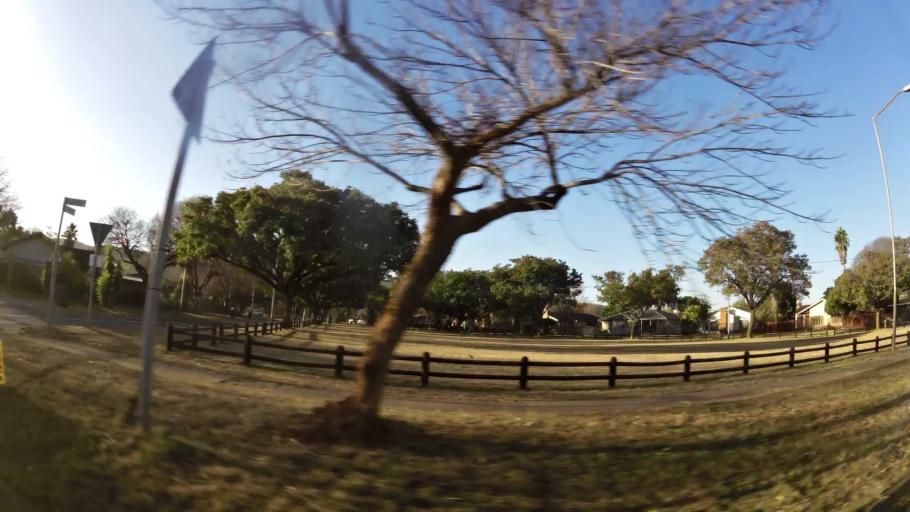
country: ZA
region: Gauteng
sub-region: City of Tshwane Metropolitan Municipality
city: Pretoria
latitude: -25.7057
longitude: 28.2142
